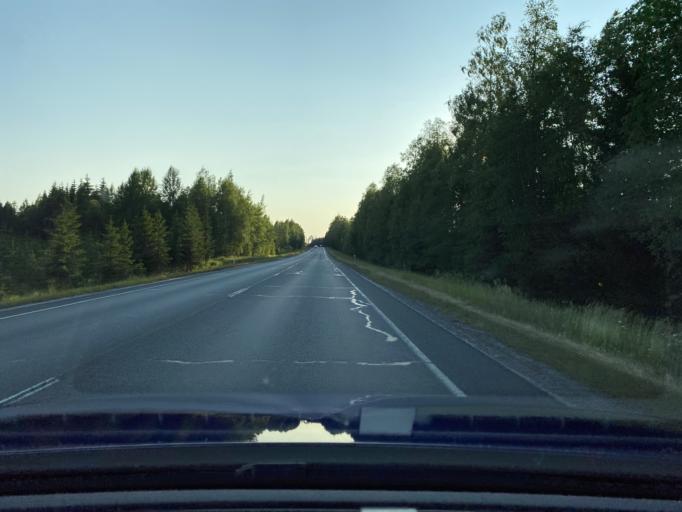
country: FI
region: Haeme
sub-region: Forssa
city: Tammela
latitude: 60.8282
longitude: 23.8910
